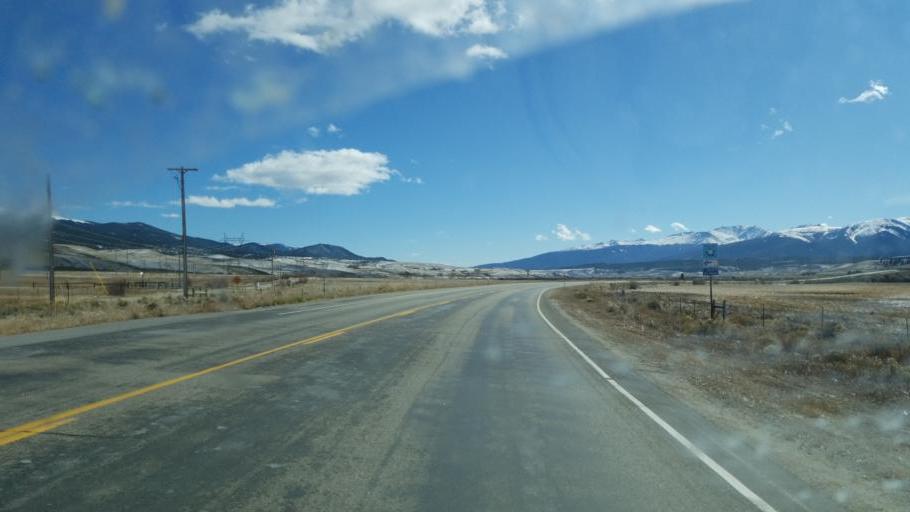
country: US
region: Colorado
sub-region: Lake County
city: Leadville
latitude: 39.1763
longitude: -106.3222
